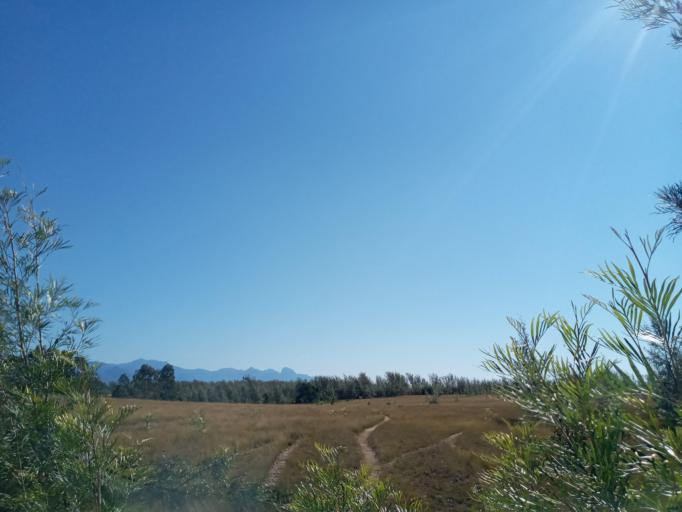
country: MG
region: Atsimo-Atsinanana
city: Vohipaho
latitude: -24.2470
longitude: 47.3159
